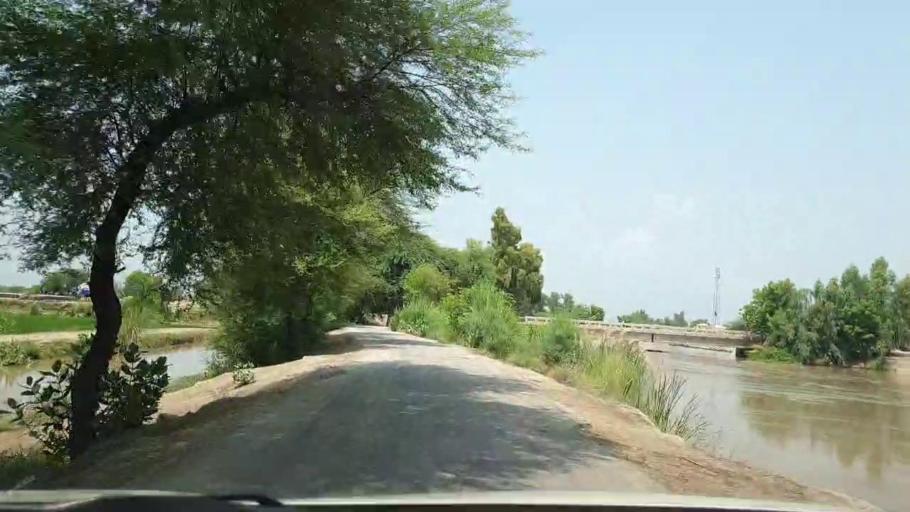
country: PK
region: Sindh
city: Dokri
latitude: 27.3642
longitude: 68.1143
